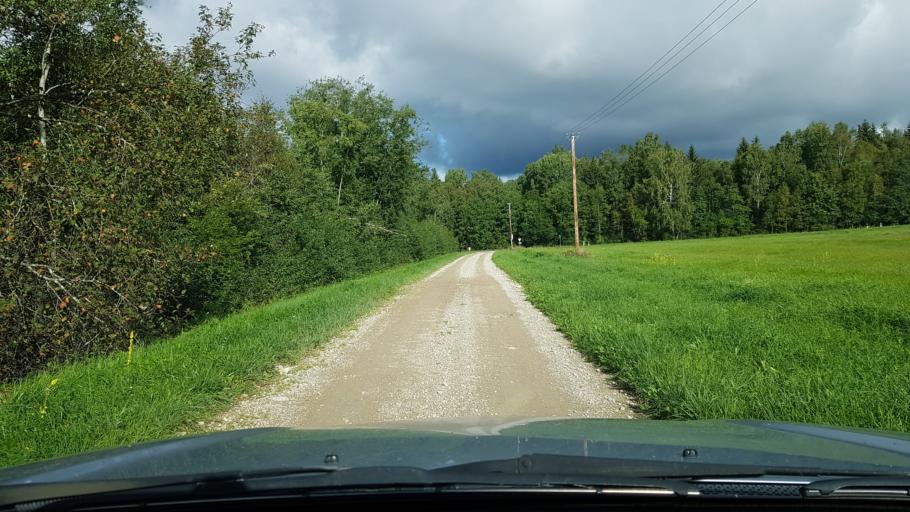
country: EE
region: Harju
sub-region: Rae vald
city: Vaida
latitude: 59.2576
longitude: 25.0531
